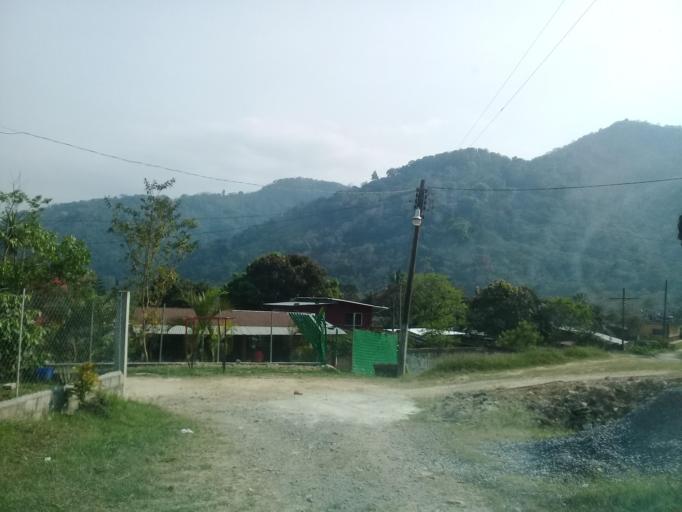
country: MX
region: Veracruz
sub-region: Ixtaczoquitlan
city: Campo Chico
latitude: 18.8388
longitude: -97.0305
